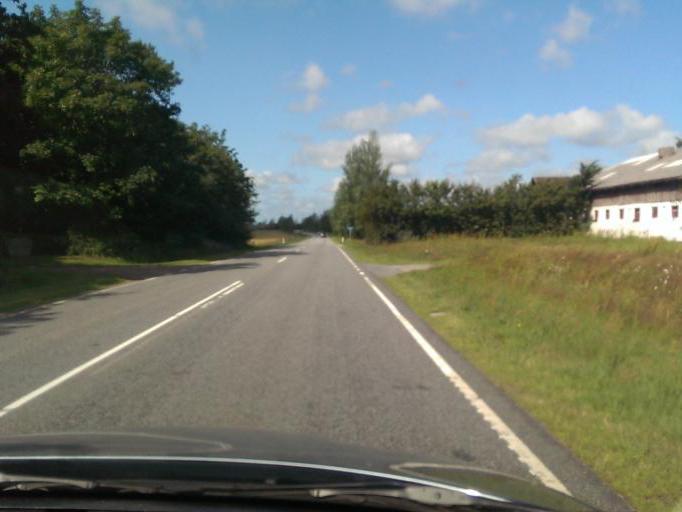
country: DK
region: North Denmark
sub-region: Bronderslev Kommune
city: Bronderslev
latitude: 57.2098
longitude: 9.9109
